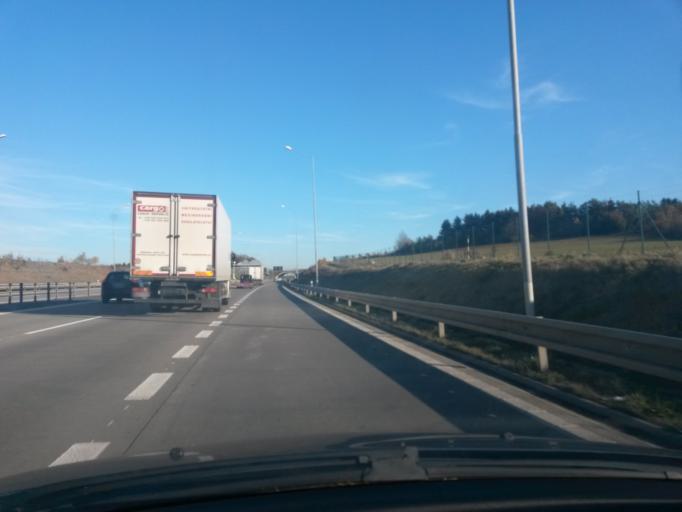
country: CZ
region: Central Bohemia
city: Jesenice
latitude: 49.9625
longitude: 14.5283
